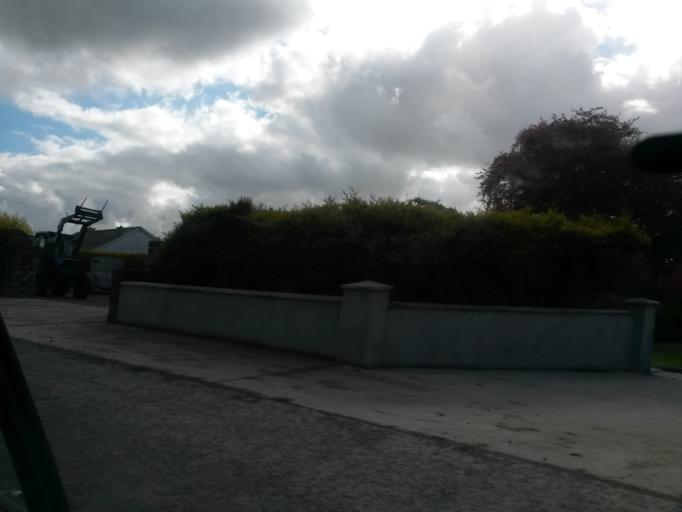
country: IE
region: Leinster
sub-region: Loch Garman
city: Ferns
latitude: 52.5728
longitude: -6.5185
